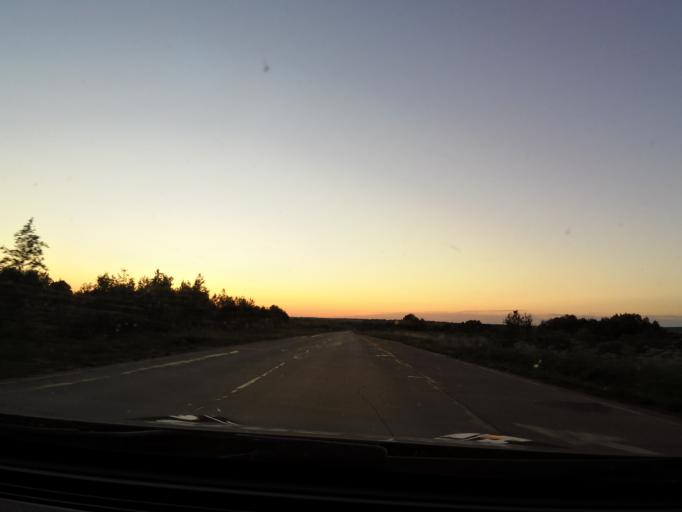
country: RU
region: Vologda
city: Vytegra
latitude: 60.8953
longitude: 36.0454
